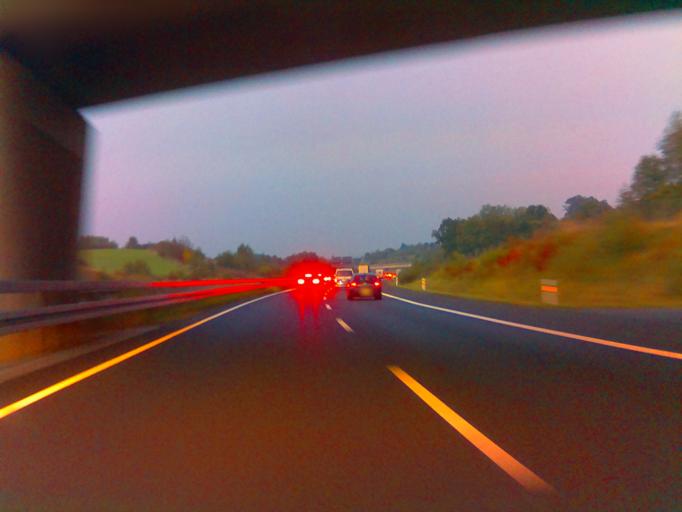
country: DE
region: Hesse
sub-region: Regierungsbezirk Kassel
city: Flieden
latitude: 50.3946
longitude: 9.5407
